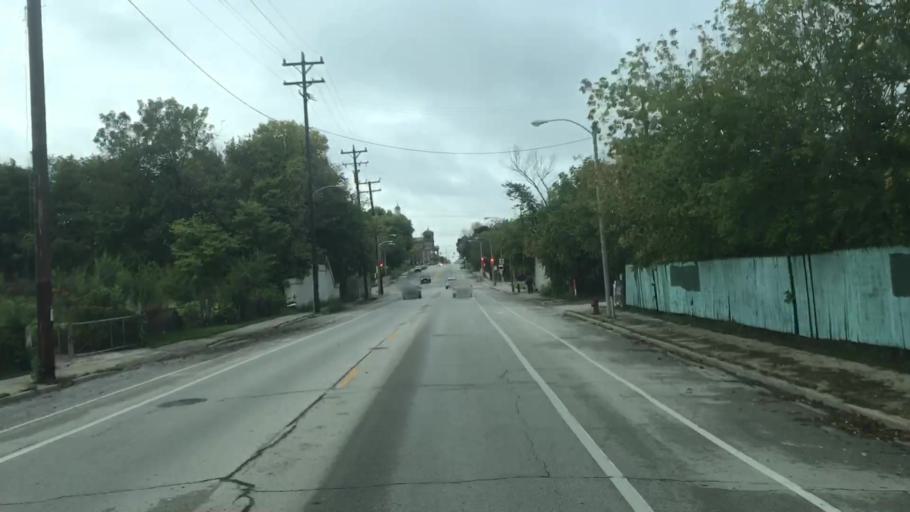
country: US
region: Wisconsin
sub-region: Milwaukee County
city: Milwaukee
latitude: 43.0029
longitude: -87.9094
